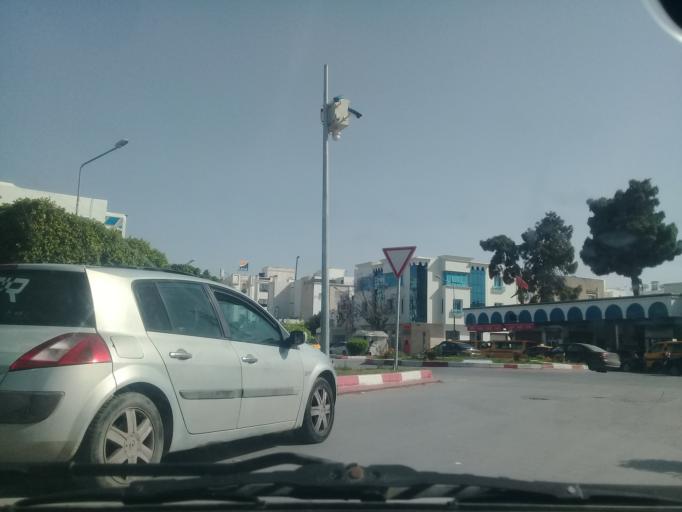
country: TN
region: Tunis
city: Al Marsa
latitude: 36.8810
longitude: 10.3269
